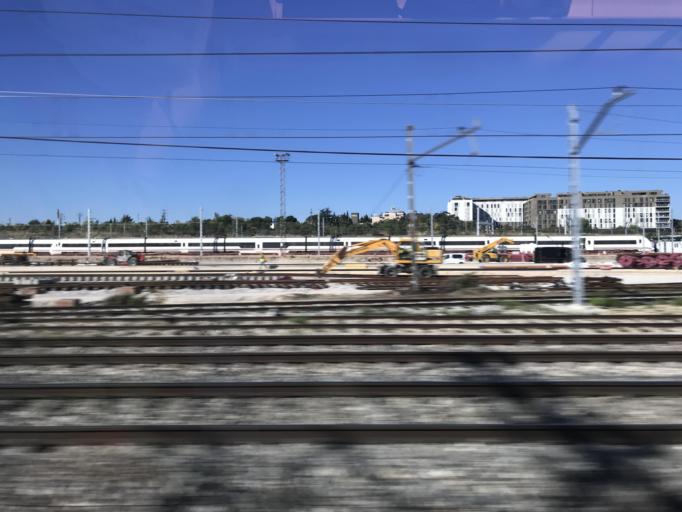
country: ES
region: Madrid
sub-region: Provincia de Madrid
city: Las Tablas
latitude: 40.5057
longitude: -3.6812
